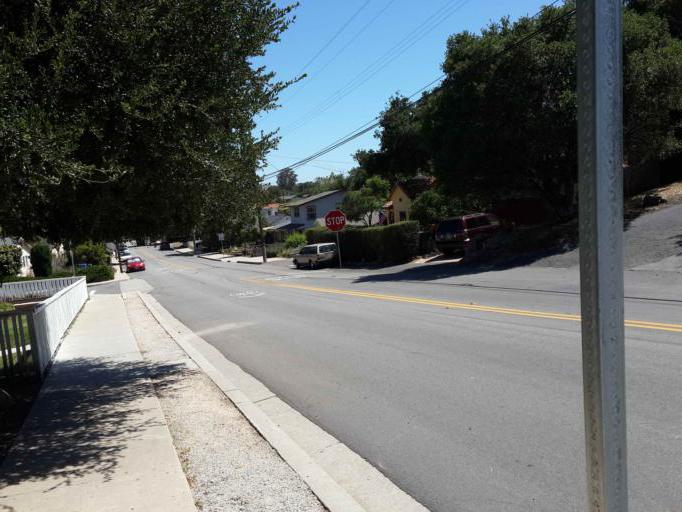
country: US
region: California
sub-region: San Luis Obispo County
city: San Luis Obispo
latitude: 35.2867
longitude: -120.6703
